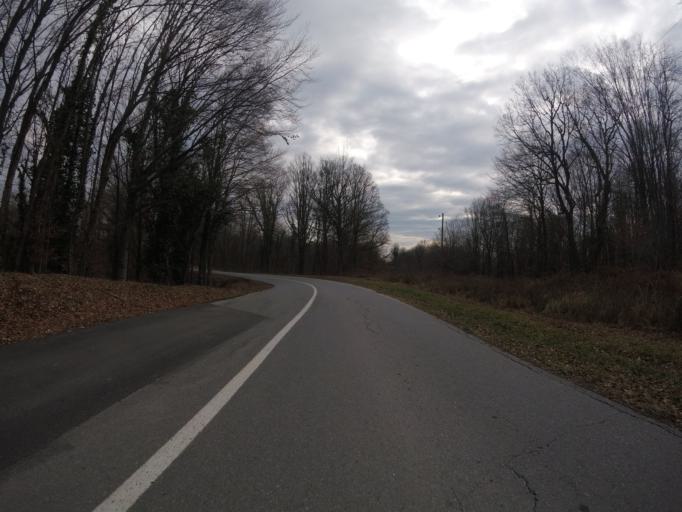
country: HR
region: Zagrebacka
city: Mraclin
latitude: 45.5449
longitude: 16.0579
